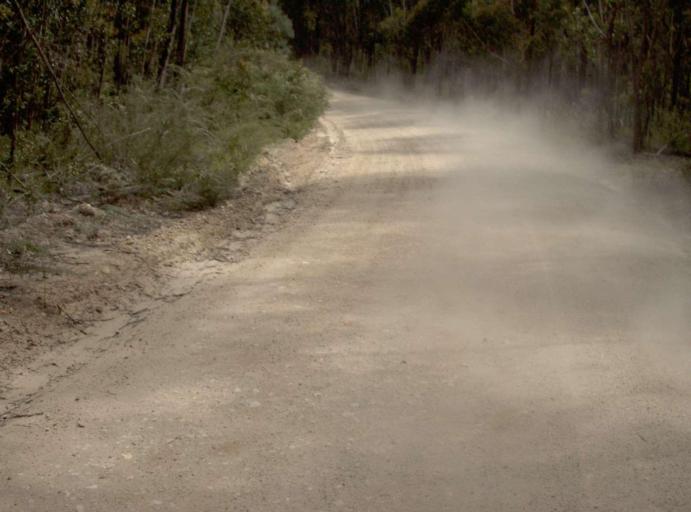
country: AU
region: Victoria
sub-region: East Gippsland
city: Lakes Entrance
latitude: -37.6770
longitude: 148.6270
